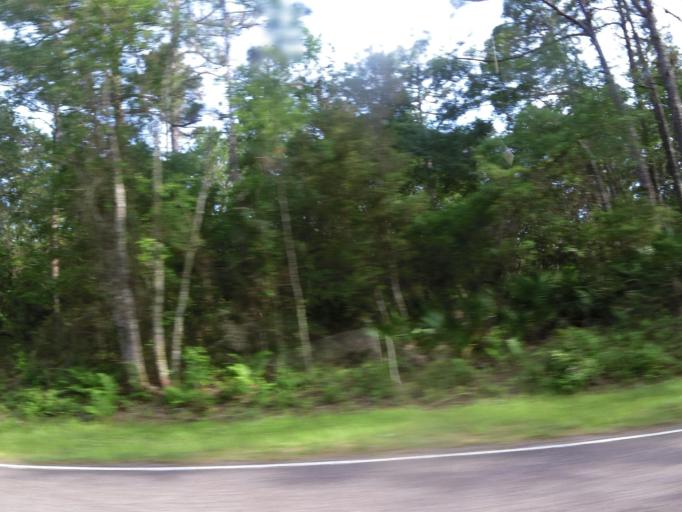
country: US
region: Florida
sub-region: Duval County
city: Atlantic Beach
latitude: 30.4623
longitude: -81.4902
